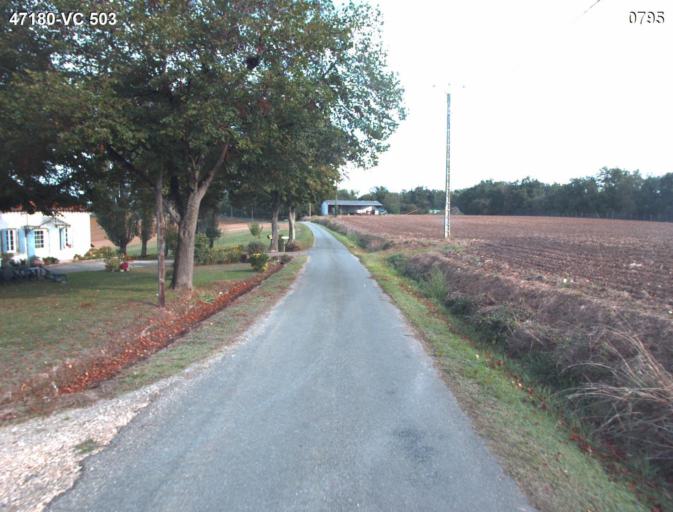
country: FR
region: Aquitaine
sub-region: Departement du Lot-et-Garonne
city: Sainte-Colombe-en-Bruilhois
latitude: 44.1766
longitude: 0.4322
